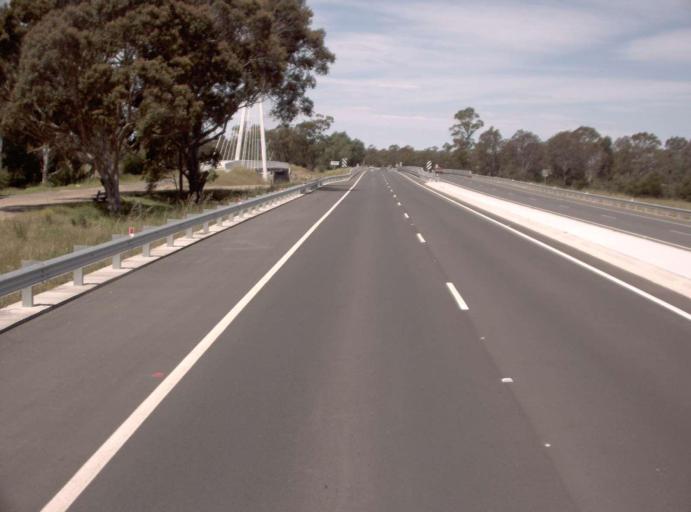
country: AU
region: Victoria
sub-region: Wellington
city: Sale
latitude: -38.1126
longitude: 147.0464
